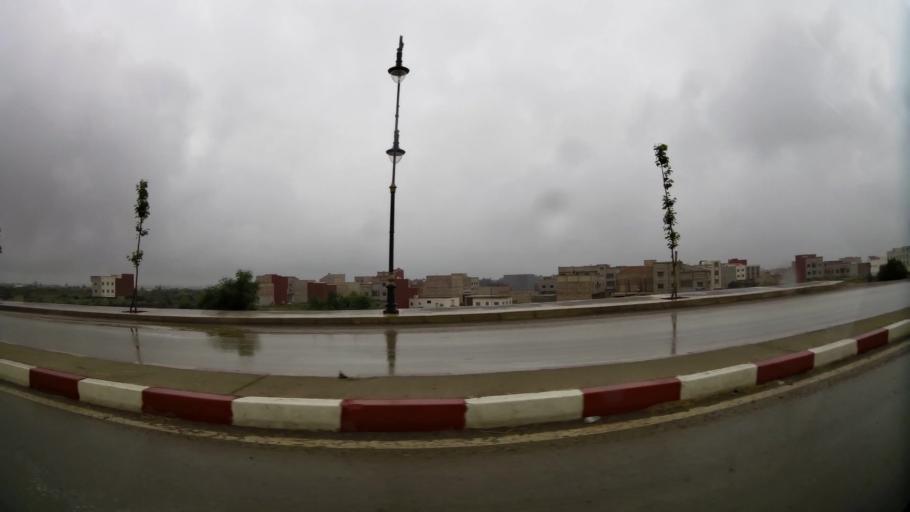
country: MA
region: Taza-Al Hoceima-Taounate
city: Imzourene
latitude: 35.1548
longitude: -3.8448
